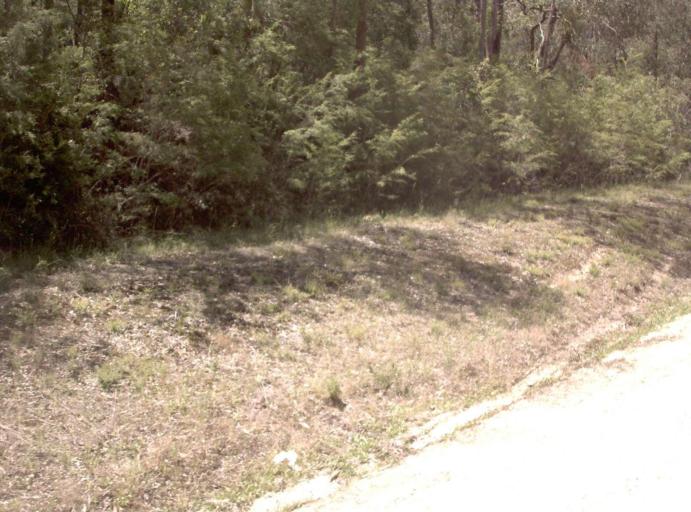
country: AU
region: New South Wales
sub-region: Bombala
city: Bombala
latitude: -37.6290
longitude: 148.8855
